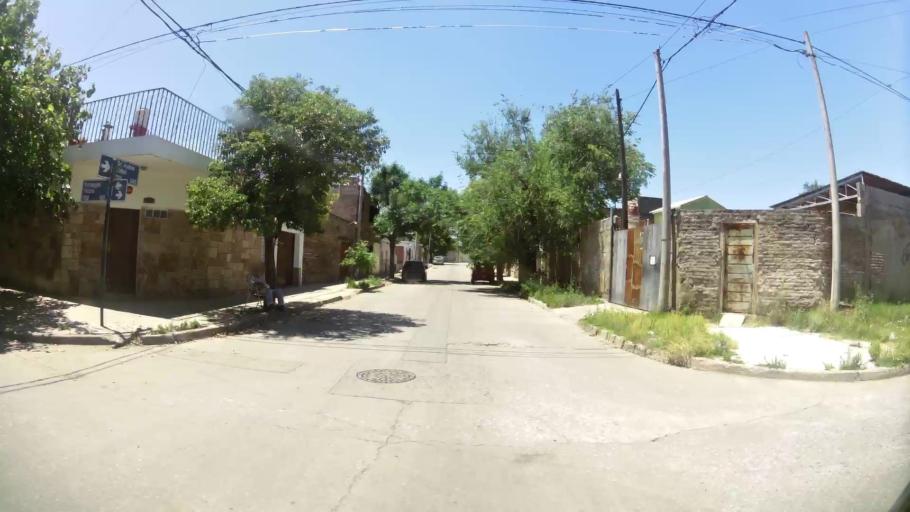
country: AR
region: Cordoba
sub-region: Departamento de Capital
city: Cordoba
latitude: -31.3967
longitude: -64.2117
